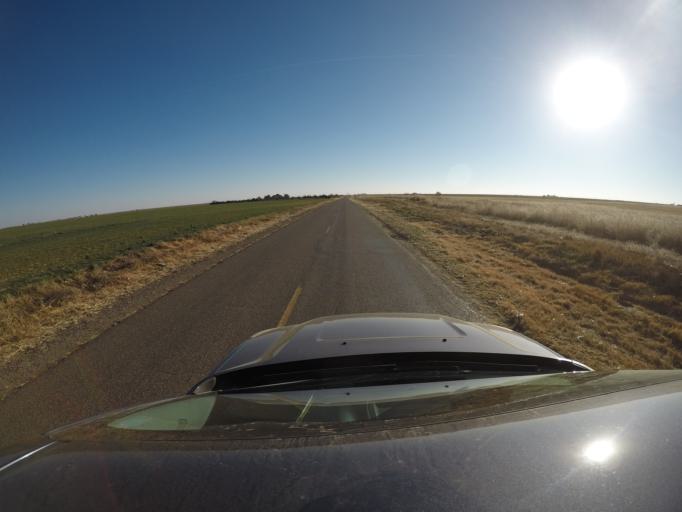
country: US
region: Texas
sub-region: Parmer County
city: Farwell
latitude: 34.3169
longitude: -103.0438
